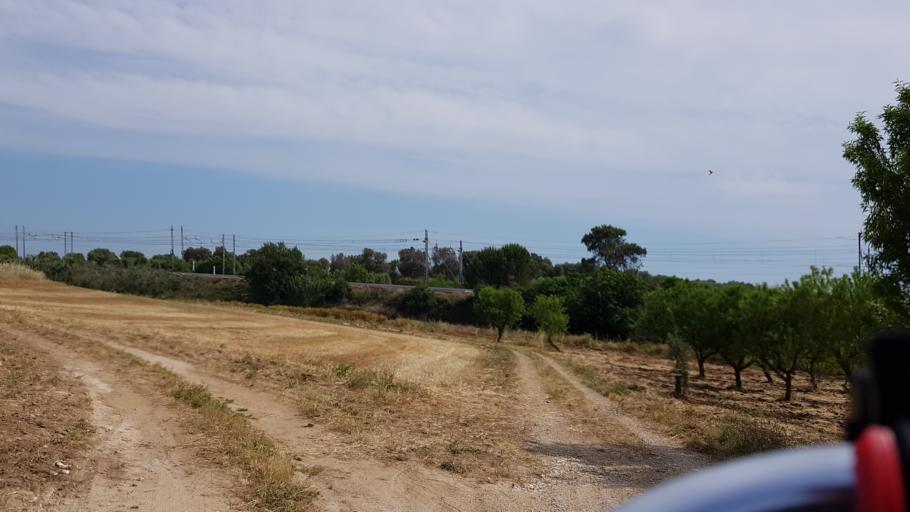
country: IT
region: Apulia
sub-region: Provincia di Brindisi
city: San Vito dei Normanni
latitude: 40.6597
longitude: 17.7995
